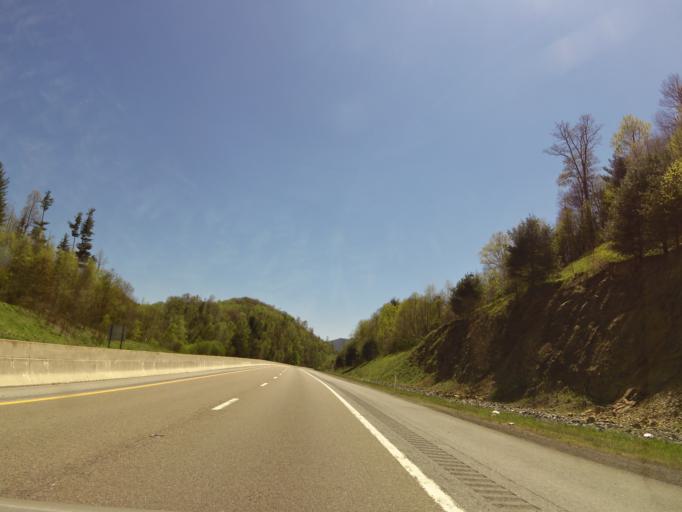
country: US
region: Tennessee
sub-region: Unicoi County
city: Banner Hill
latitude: 36.0308
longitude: -82.5406
